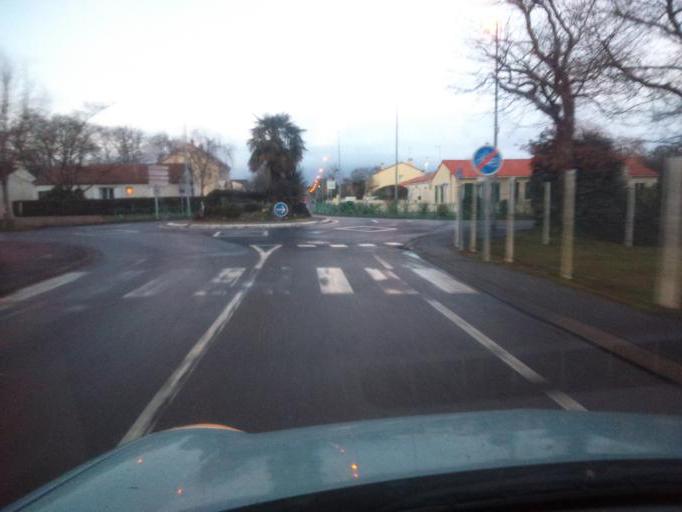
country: FR
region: Pays de la Loire
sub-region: Departement de la Loire-Atlantique
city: La Montagne
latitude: 47.1797
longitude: -1.6775
